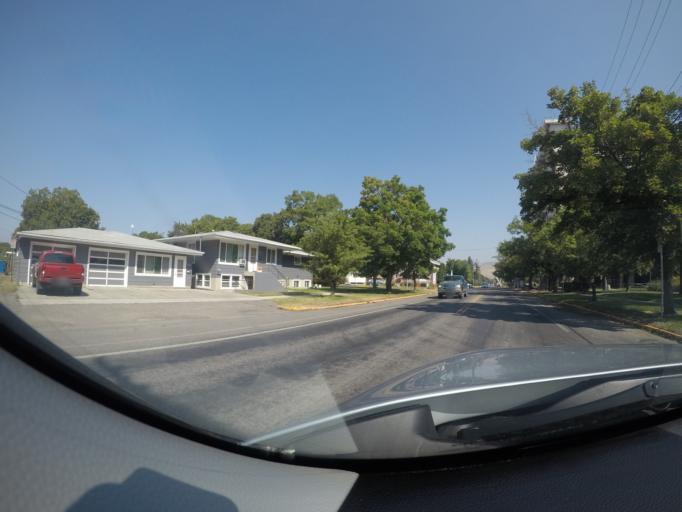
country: US
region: Montana
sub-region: Missoula County
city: Missoula
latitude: 46.8606
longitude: -113.9893
